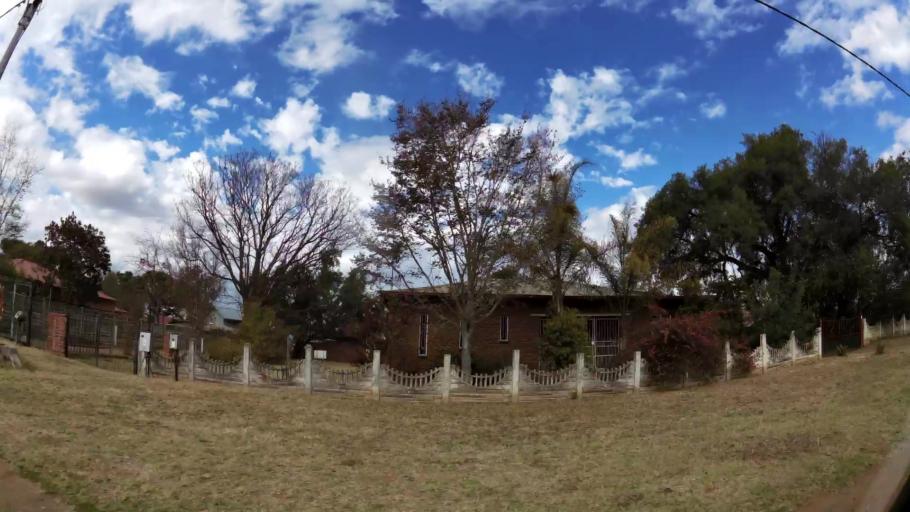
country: ZA
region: Limpopo
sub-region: Waterberg District Municipality
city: Modimolle
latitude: -24.7108
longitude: 28.4036
